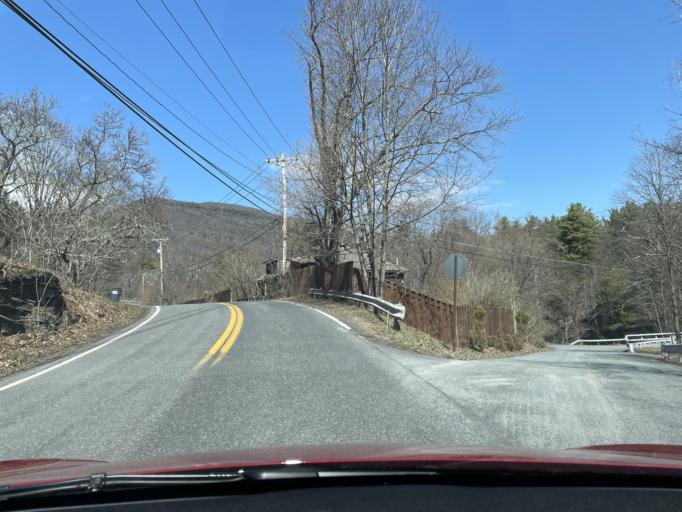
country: US
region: New York
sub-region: Ulster County
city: Manorville
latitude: 42.1116
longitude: -74.0461
